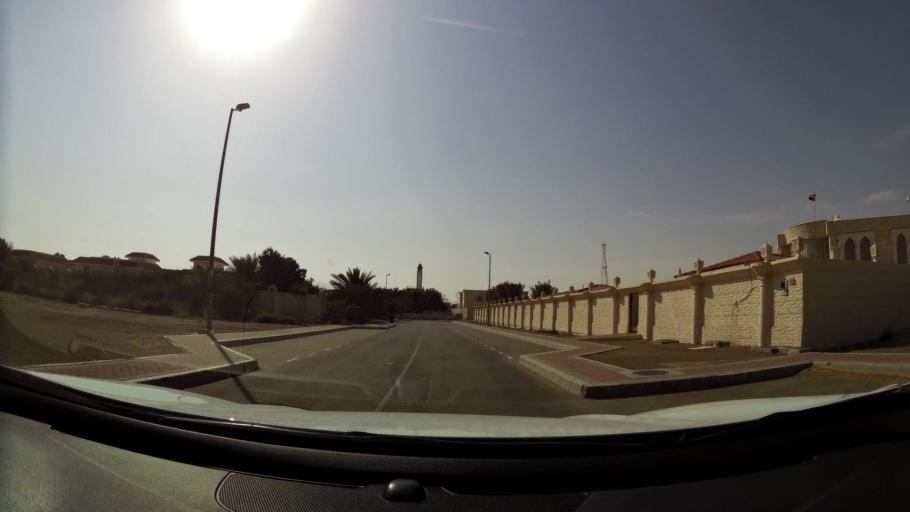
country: AE
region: Abu Dhabi
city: Al Ain
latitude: 24.0929
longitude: 55.9201
